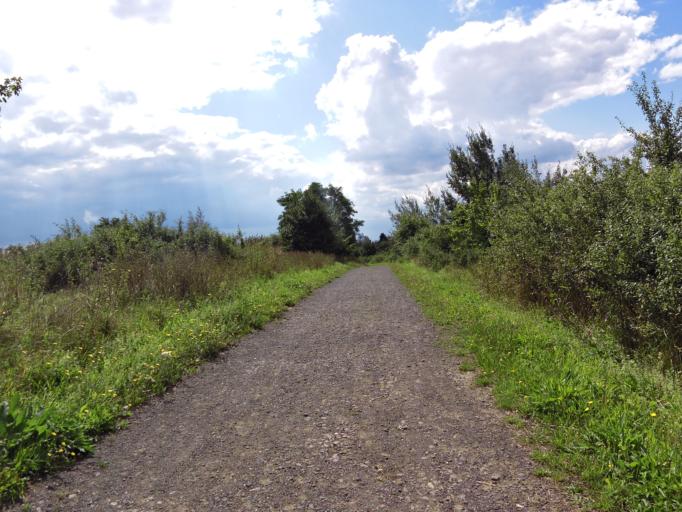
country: DE
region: Saxony
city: Rackwitz
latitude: 51.3843
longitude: 12.3971
